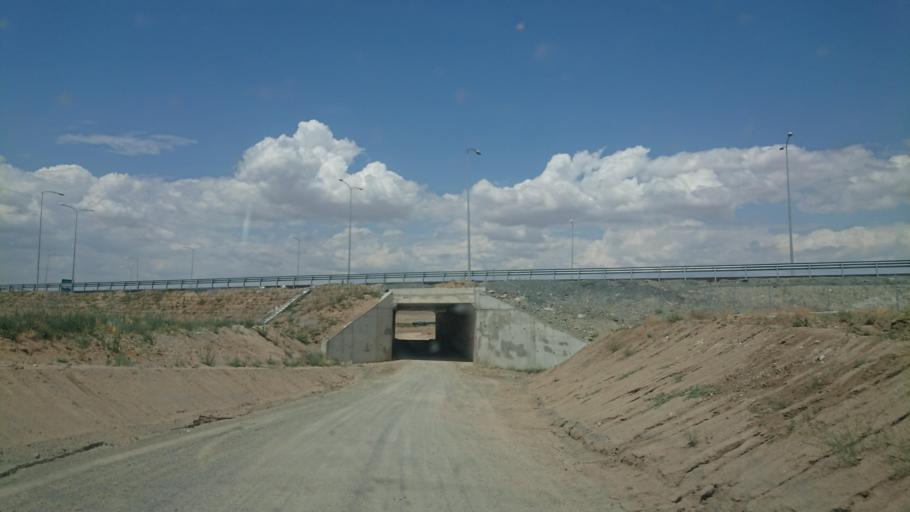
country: TR
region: Aksaray
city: Sariyahsi
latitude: 38.9737
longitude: 33.8990
